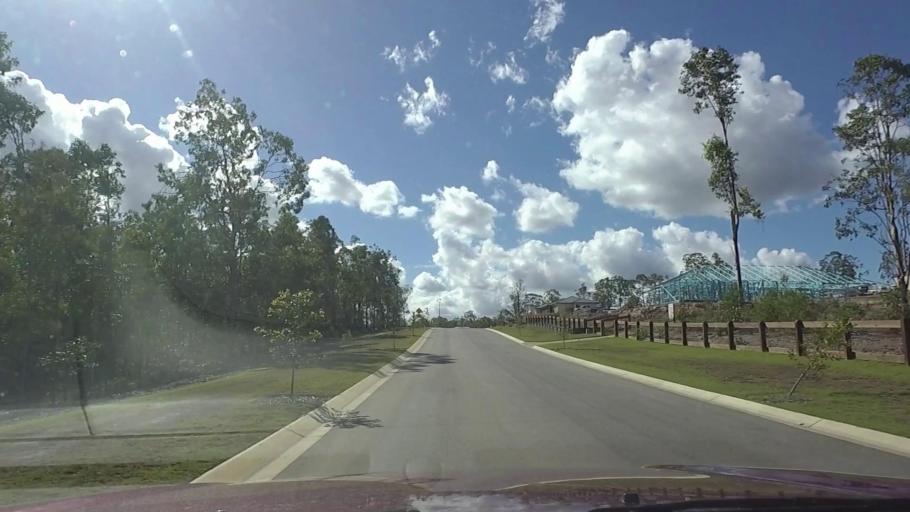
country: AU
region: Queensland
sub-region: Ipswich
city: Springfield Lakes
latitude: -27.7539
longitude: 152.9192
